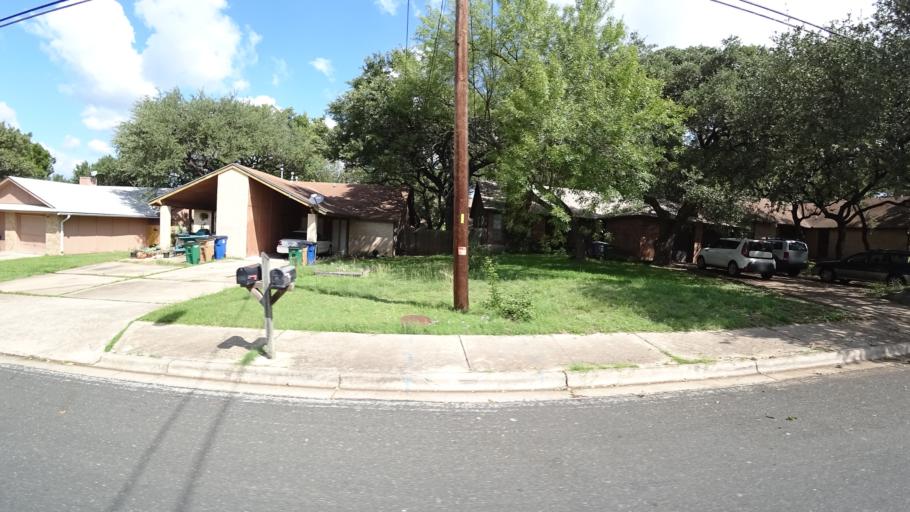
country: US
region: Texas
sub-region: Travis County
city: Onion Creek
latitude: 30.1978
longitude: -97.8027
